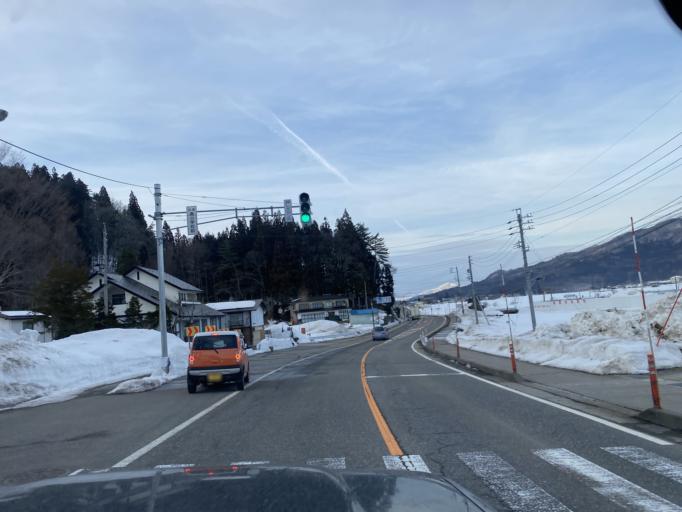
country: JP
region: Nagano
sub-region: Kitaazumi Gun
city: Hakuba
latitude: 36.6463
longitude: 137.8444
